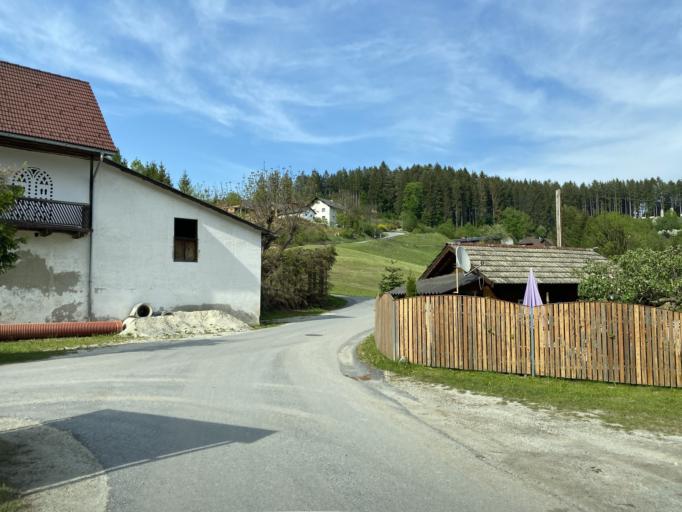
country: AT
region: Styria
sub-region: Politischer Bezirk Weiz
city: Birkfeld
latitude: 47.3589
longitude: 15.6883
